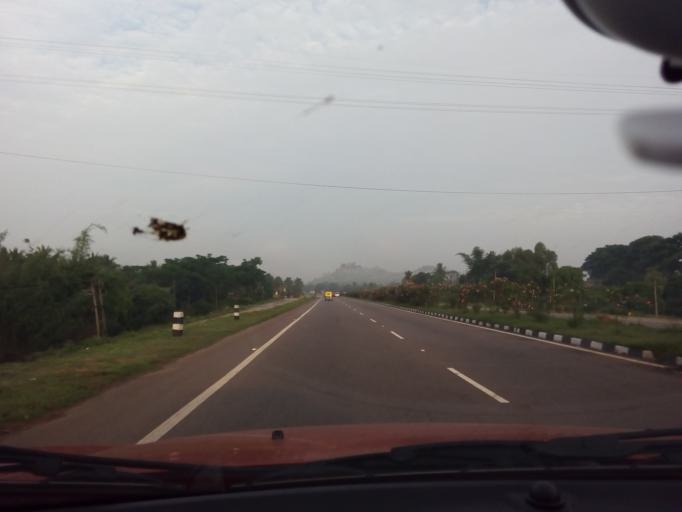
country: IN
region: Karnataka
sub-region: Ramanagara
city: Magadi
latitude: 13.0762
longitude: 77.2037
